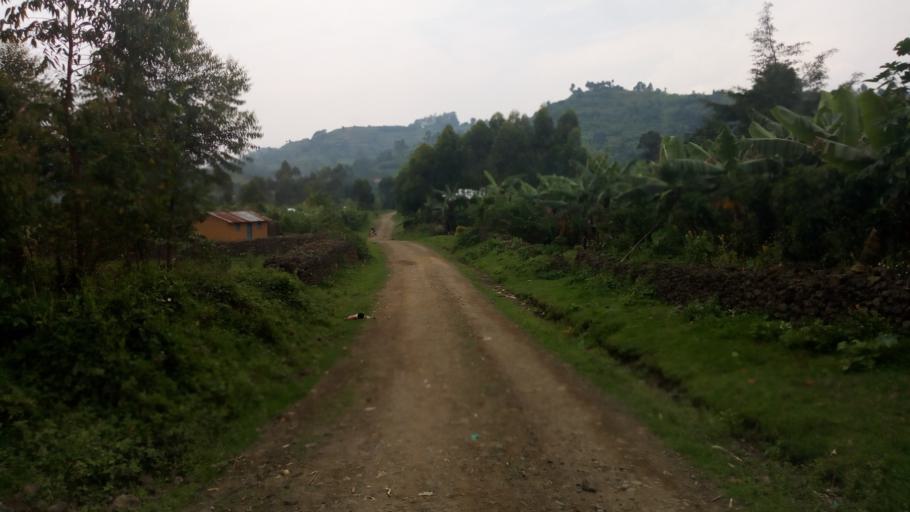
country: UG
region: Western Region
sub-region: Kisoro District
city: Kisoro
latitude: -1.2630
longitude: 29.6271
